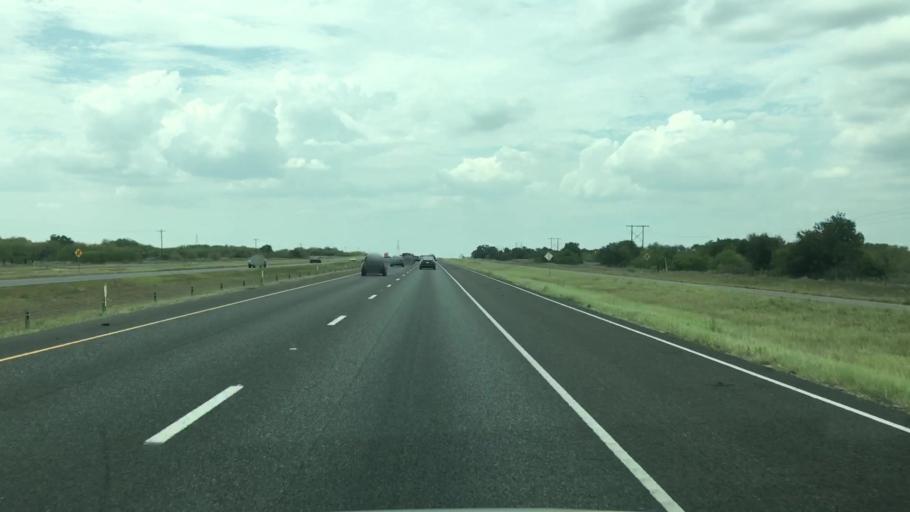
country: US
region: Texas
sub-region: Atascosa County
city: Pleasanton
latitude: 28.8100
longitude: -98.3509
